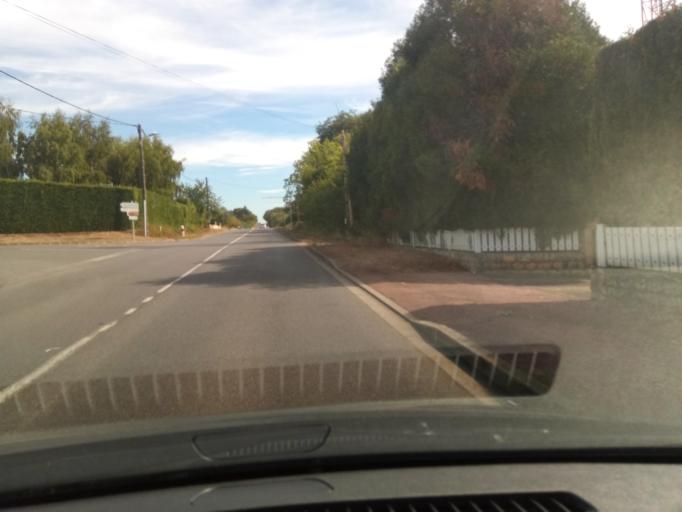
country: FR
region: Poitou-Charentes
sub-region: Departement de la Vienne
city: Chauvigny
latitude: 46.5585
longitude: 0.6496
